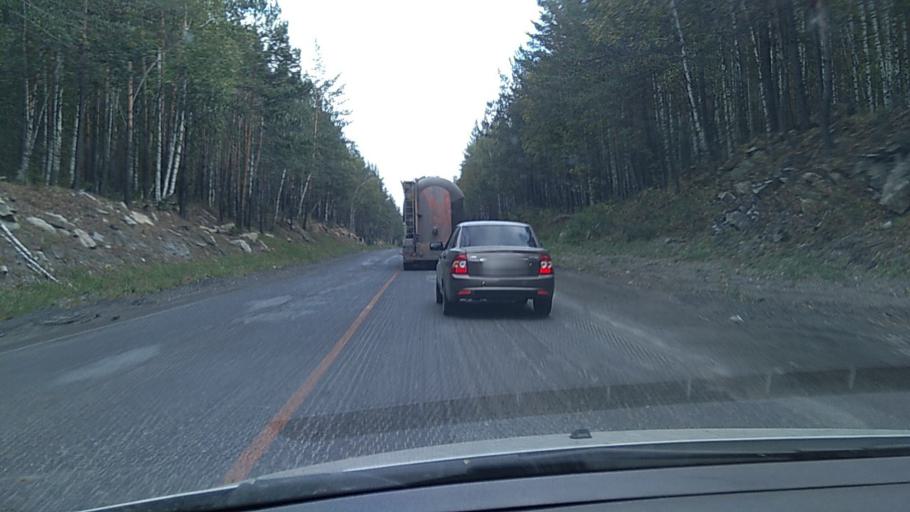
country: RU
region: Chelyabinsk
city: Miass
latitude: 54.9309
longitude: 60.1624
